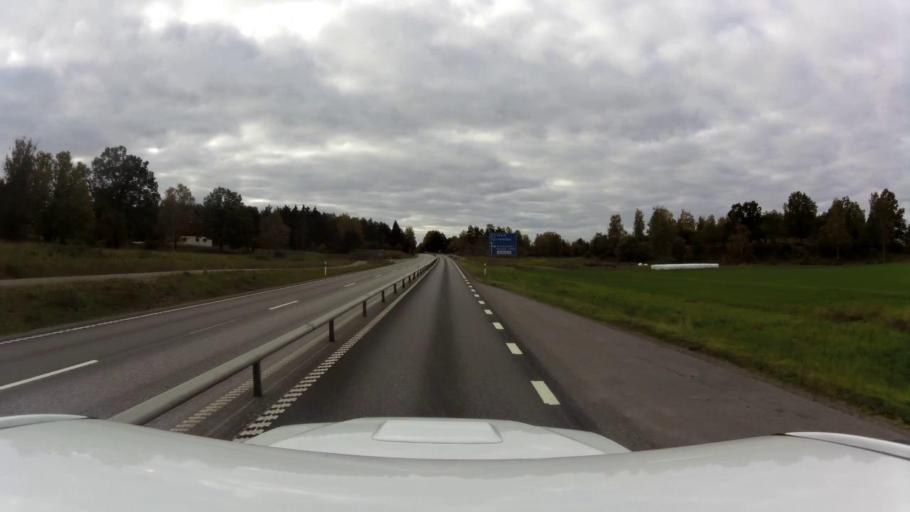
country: SE
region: OEstergoetland
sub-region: Linkopings Kommun
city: Malmslatt
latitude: 58.3063
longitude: 15.5653
